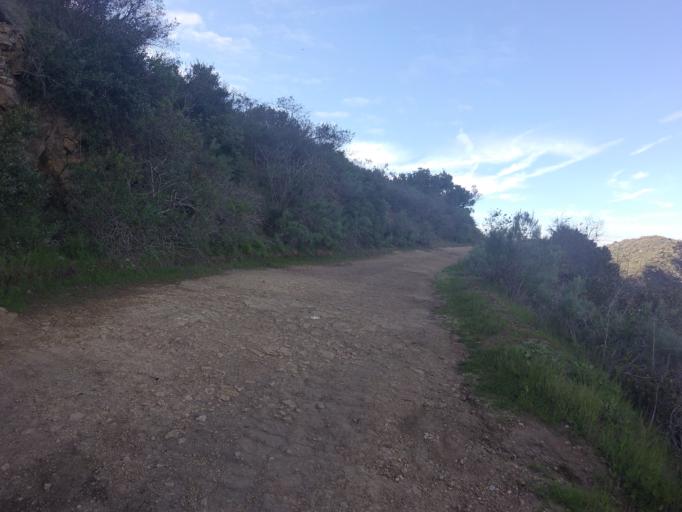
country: US
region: California
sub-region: Orange County
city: Laguna Beach
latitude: 33.5907
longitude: -117.7725
